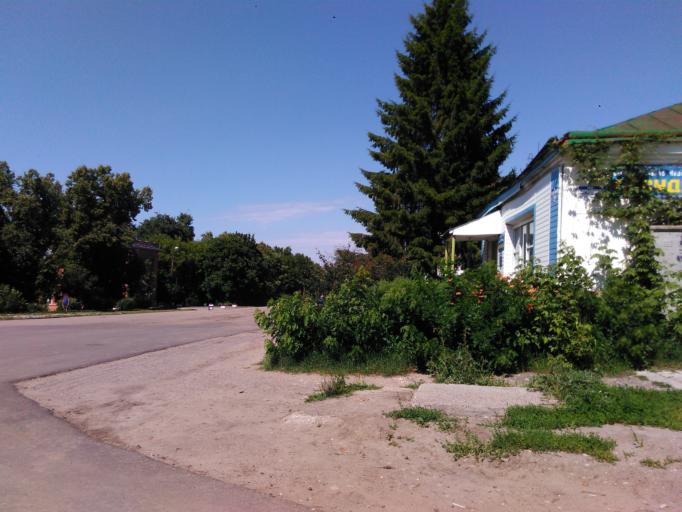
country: RU
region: Penza
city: Belinskiy
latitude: 52.9668
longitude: 43.4208
